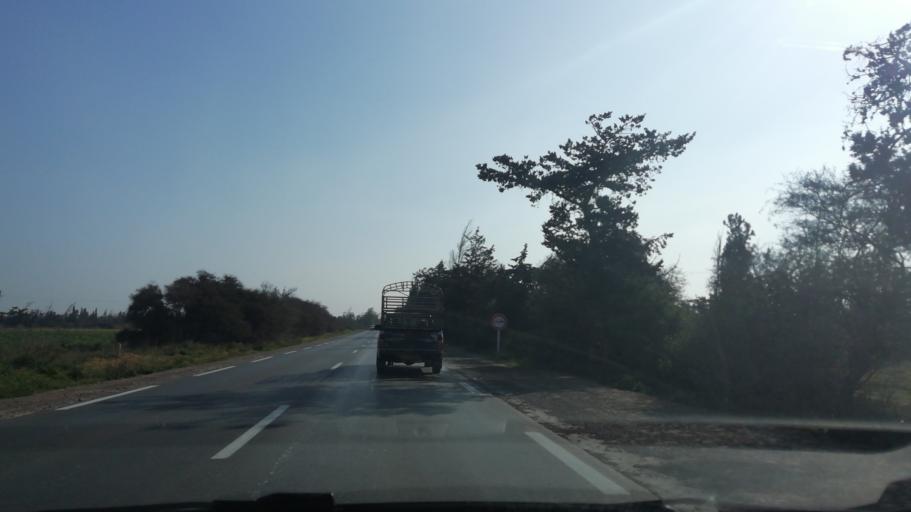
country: DZ
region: Mostaganem
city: Mostaganem
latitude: 35.7433
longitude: -0.0168
